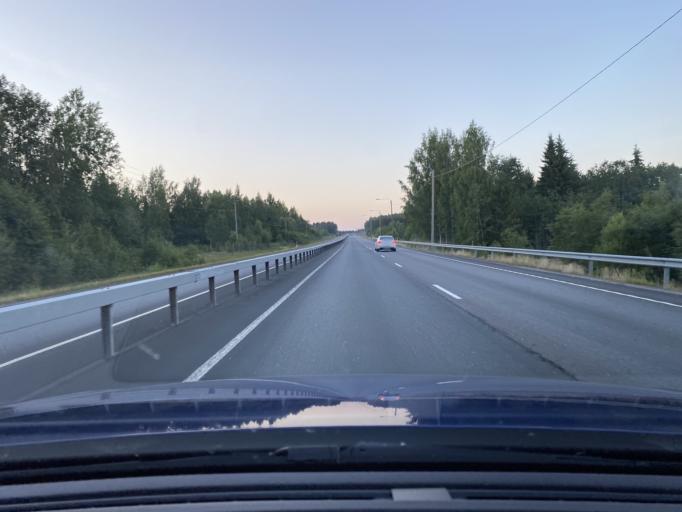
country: FI
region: Pirkanmaa
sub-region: Luoteis-Pirkanmaa
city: Parkano
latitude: 61.8825
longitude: 22.9722
